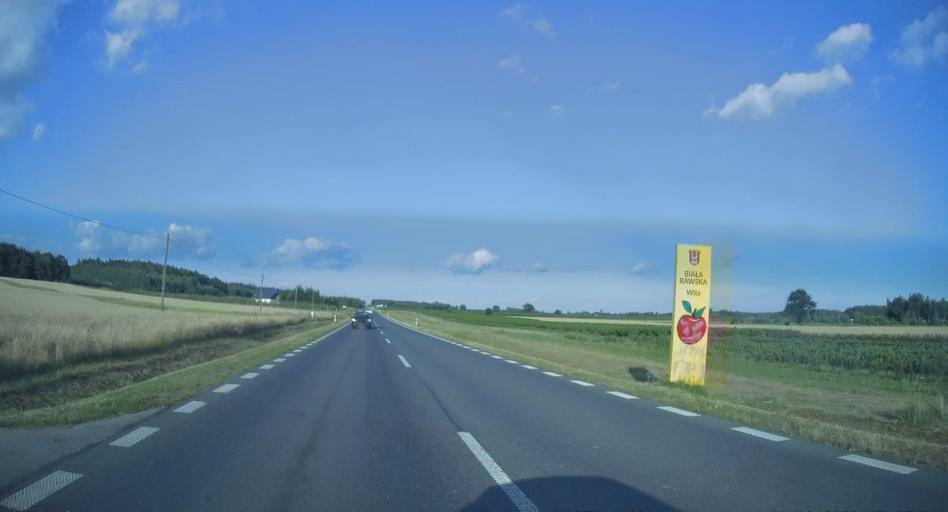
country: PL
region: Lodz Voivodeship
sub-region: Powiat rawski
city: Regnow
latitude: 51.7870
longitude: 20.3432
